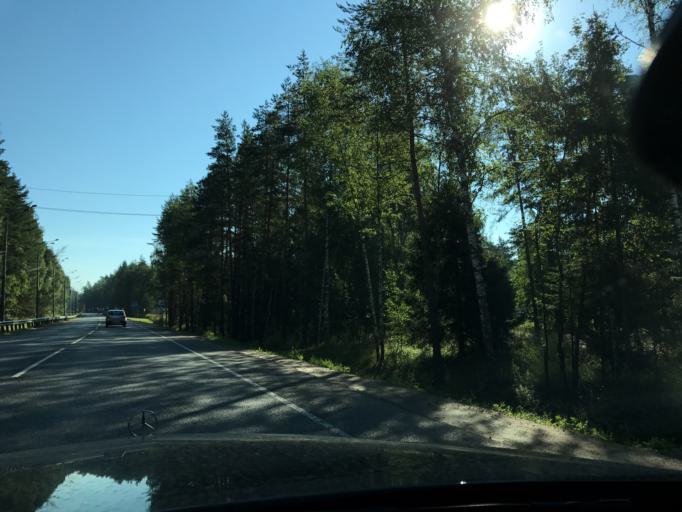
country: RU
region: Moskovskaya
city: Chernogolovka
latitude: 55.9822
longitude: 38.3292
